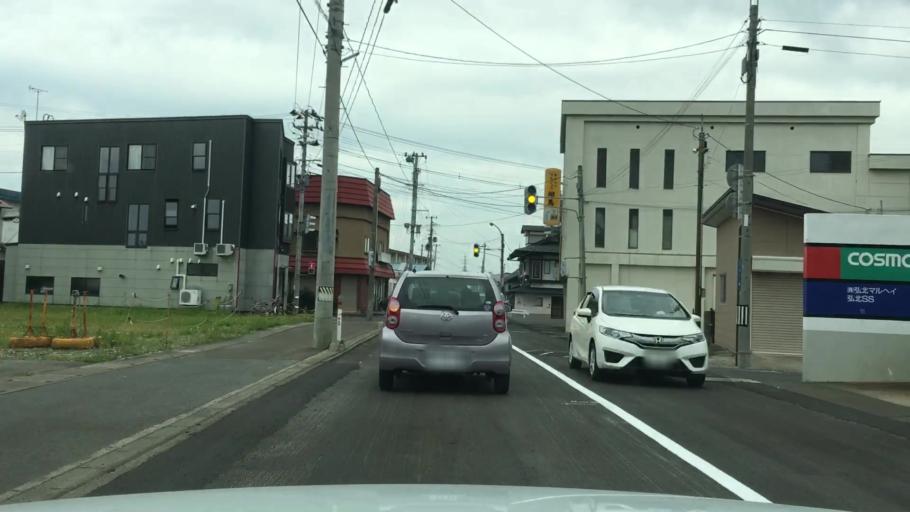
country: JP
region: Aomori
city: Hirosaki
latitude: 40.6284
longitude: 140.4538
